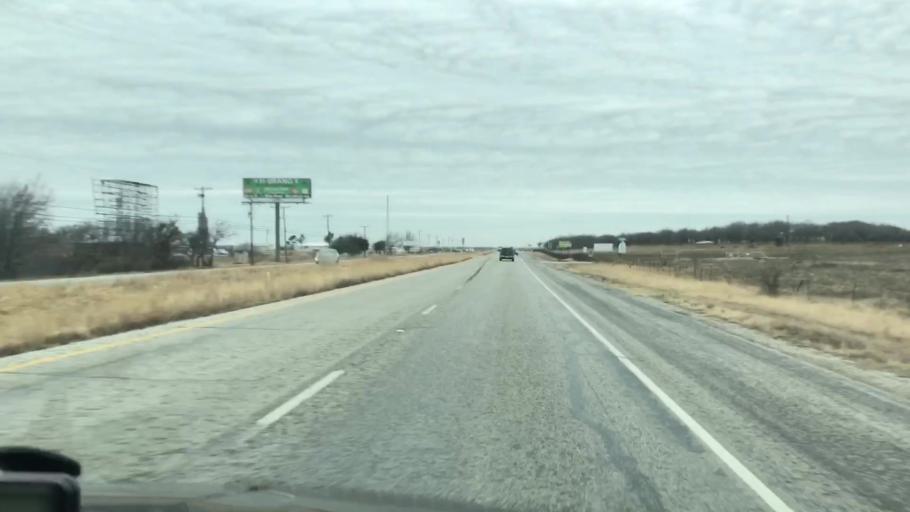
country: US
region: Texas
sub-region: Jack County
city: Jacksboro
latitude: 33.1923
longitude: -98.1392
